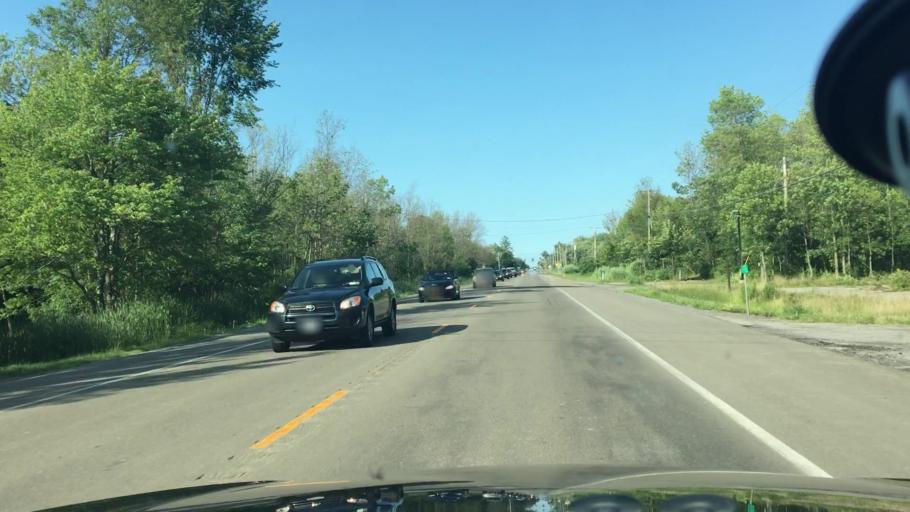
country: US
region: New York
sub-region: Erie County
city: Wanakah
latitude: 42.7049
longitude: -78.9234
